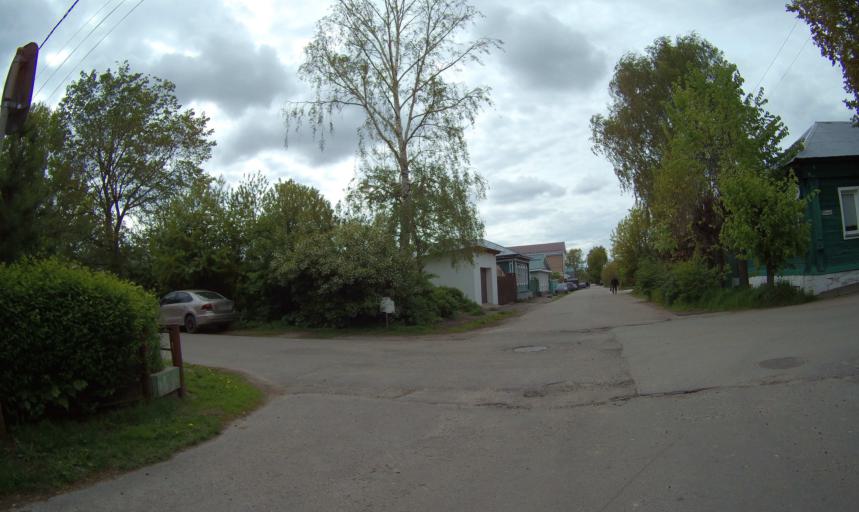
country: RU
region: Moskovskaya
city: Kolomna
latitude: 55.0991
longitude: 38.7486
